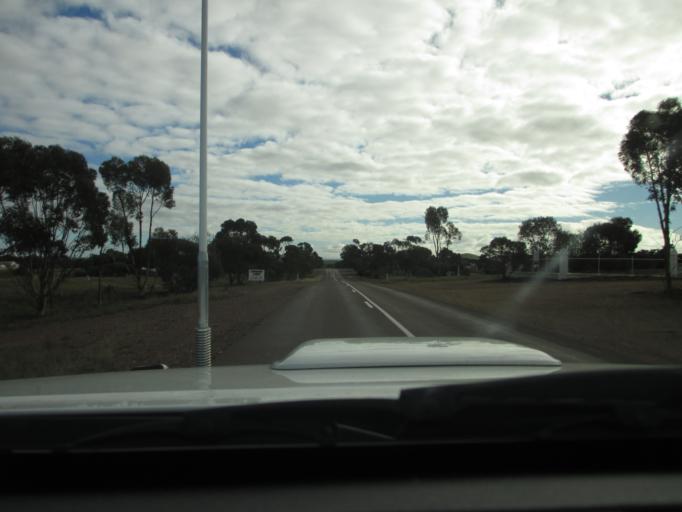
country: AU
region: South Australia
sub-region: Flinders Ranges
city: Quorn
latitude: -32.4268
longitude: 138.5310
